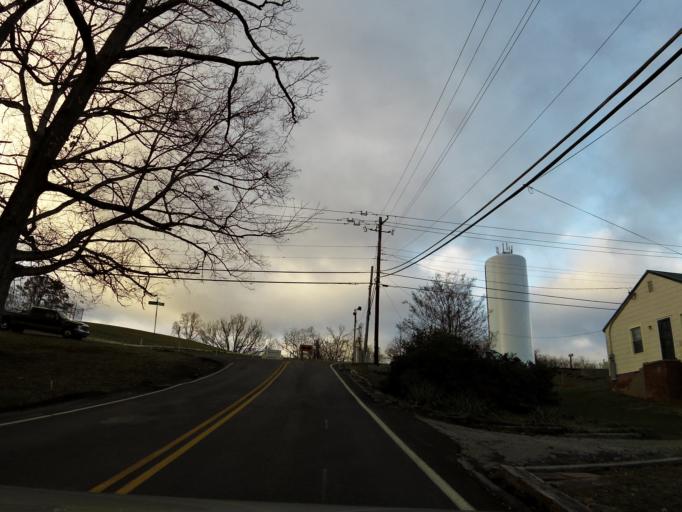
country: US
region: Tennessee
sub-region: Knox County
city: Knoxville
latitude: 36.0115
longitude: -83.8932
